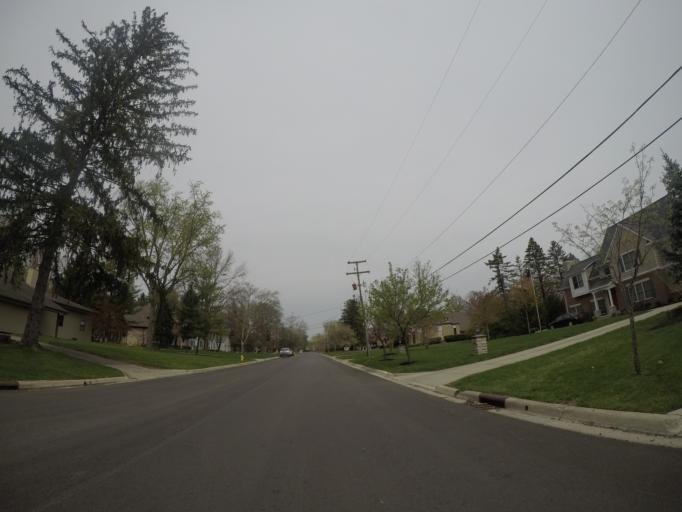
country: US
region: Ohio
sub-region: Franklin County
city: Upper Arlington
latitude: 40.0162
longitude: -83.0759
